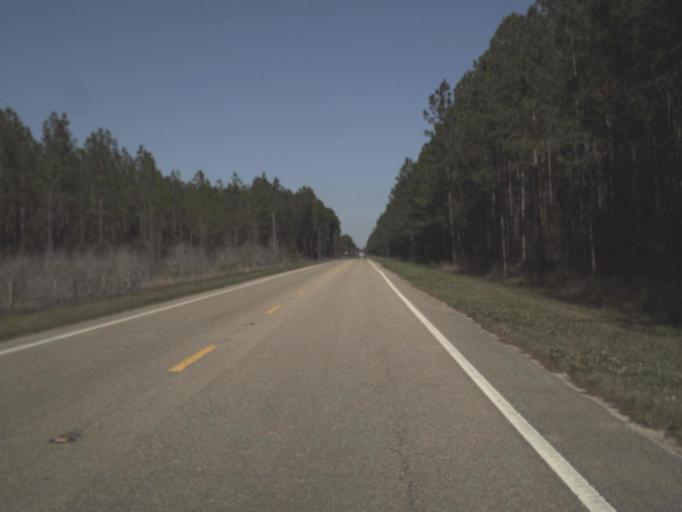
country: US
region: Florida
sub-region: Gulf County
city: Port Saint Joe
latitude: 29.8505
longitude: -85.2572
